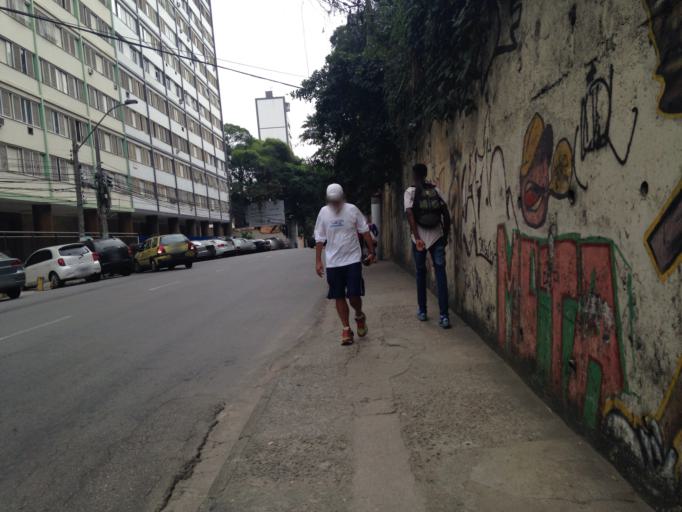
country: BR
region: Rio de Janeiro
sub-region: Niteroi
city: Niteroi
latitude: -22.9004
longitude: -43.1222
